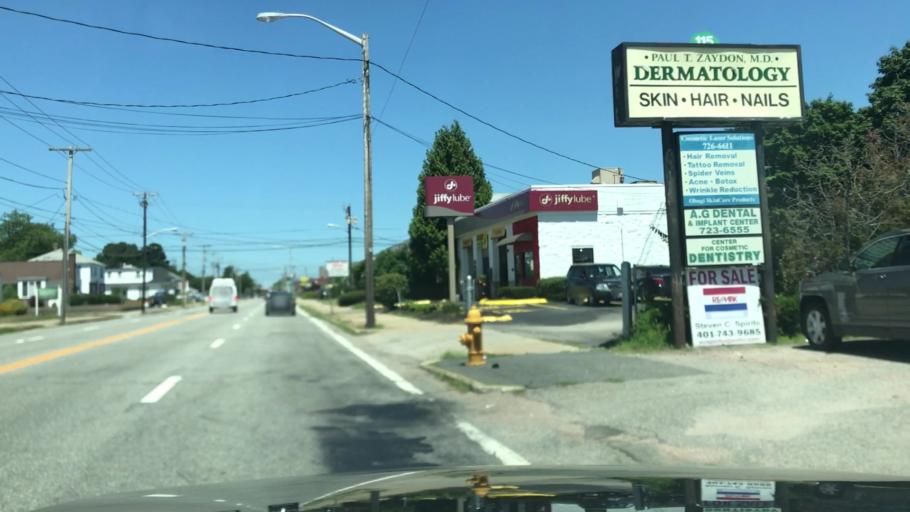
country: US
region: Rhode Island
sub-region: Providence County
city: Pawtucket
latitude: 41.8619
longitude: -71.3544
